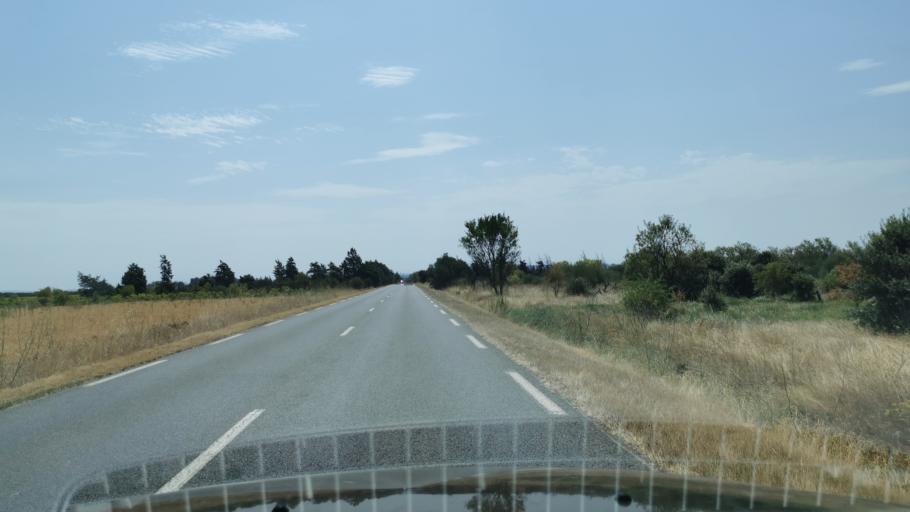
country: FR
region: Languedoc-Roussillon
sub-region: Departement de l'Aude
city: Ginestas
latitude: 43.2730
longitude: 2.8898
